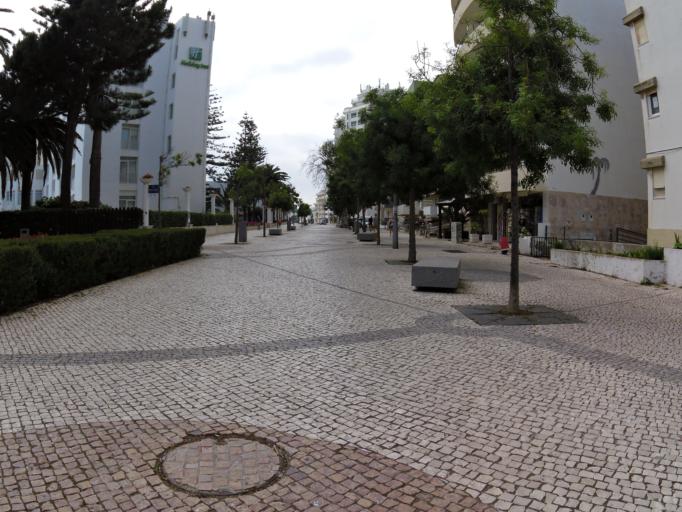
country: PT
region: Faro
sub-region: Silves
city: Armacao de Pera
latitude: 37.1022
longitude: -8.3651
